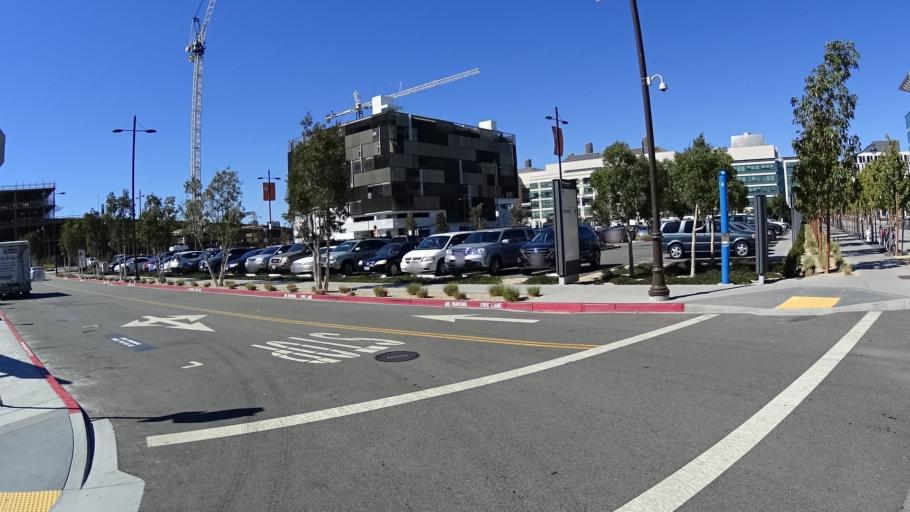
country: US
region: California
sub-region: San Francisco County
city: San Francisco
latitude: 37.7650
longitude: -122.3908
